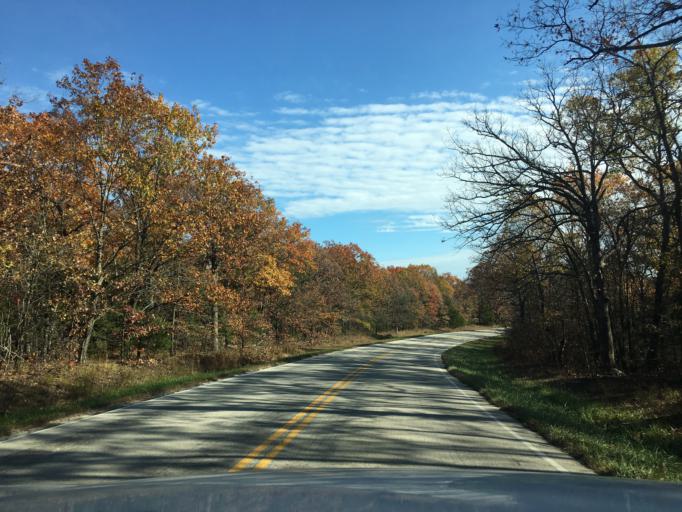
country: US
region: Missouri
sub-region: Maries County
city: Belle
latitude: 38.3171
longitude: -91.7496
